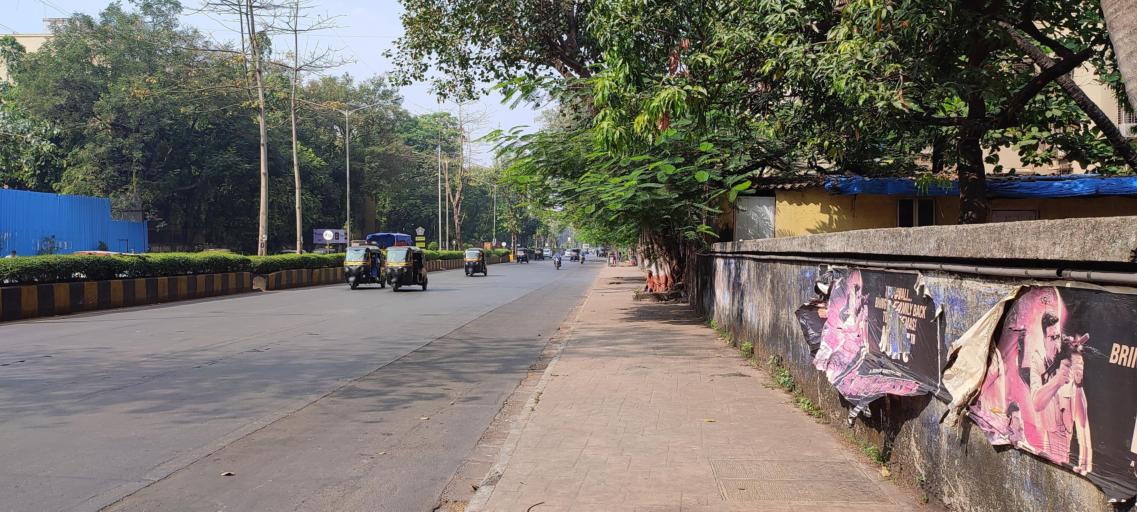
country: IN
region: Maharashtra
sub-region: Mumbai Suburban
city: Mumbai
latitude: 19.1177
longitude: 72.8292
